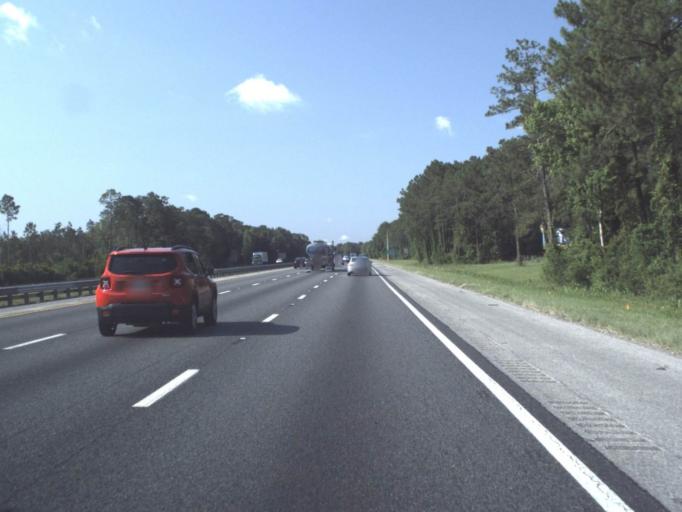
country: US
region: Florida
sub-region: Saint Johns County
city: Fruit Cove
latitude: 30.0554
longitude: -81.4977
